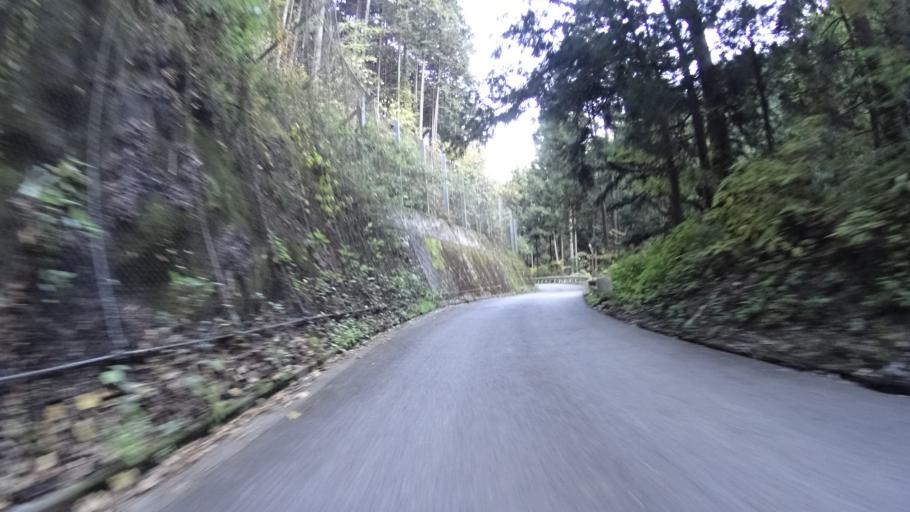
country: JP
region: Yamanashi
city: Uenohara
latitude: 35.6591
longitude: 139.1739
